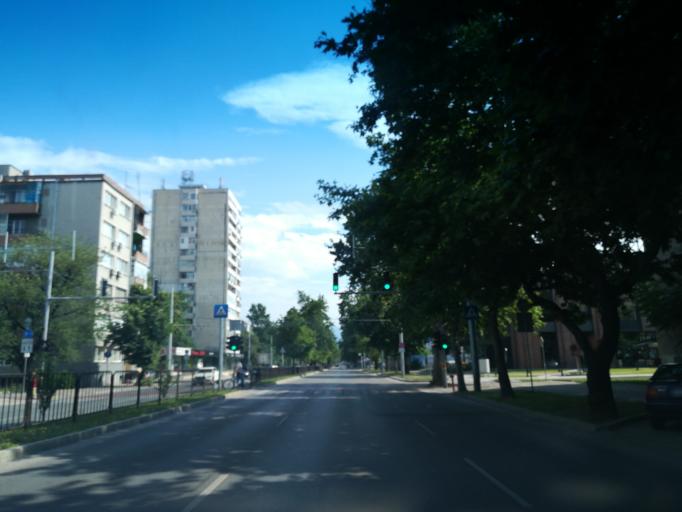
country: BG
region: Plovdiv
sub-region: Obshtina Plovdiv
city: Plovdiv
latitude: 42.1444
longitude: 24.7631
